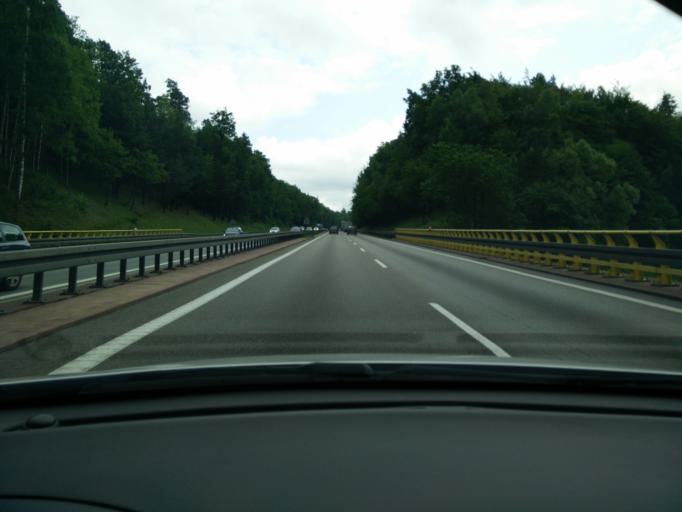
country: PL
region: Pomeranian Voivodeship
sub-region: Gdynia
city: Wielki Kack
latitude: 54.4560
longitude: 18.4904
